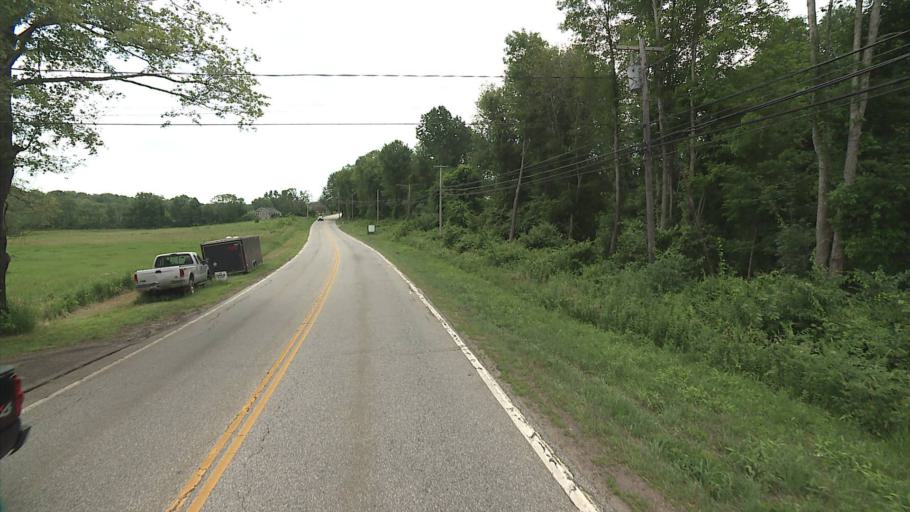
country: US
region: Connecticut
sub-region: New London County
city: Jewett City
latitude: 41.5826
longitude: -71.9779
